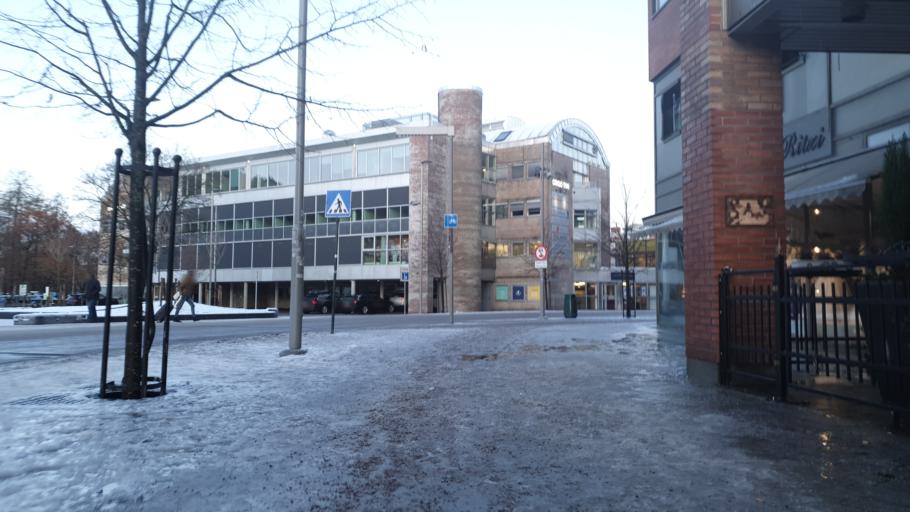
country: NO
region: Buskerud
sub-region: Drammen
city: Drammen
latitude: 59.7384
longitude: 10.2021
